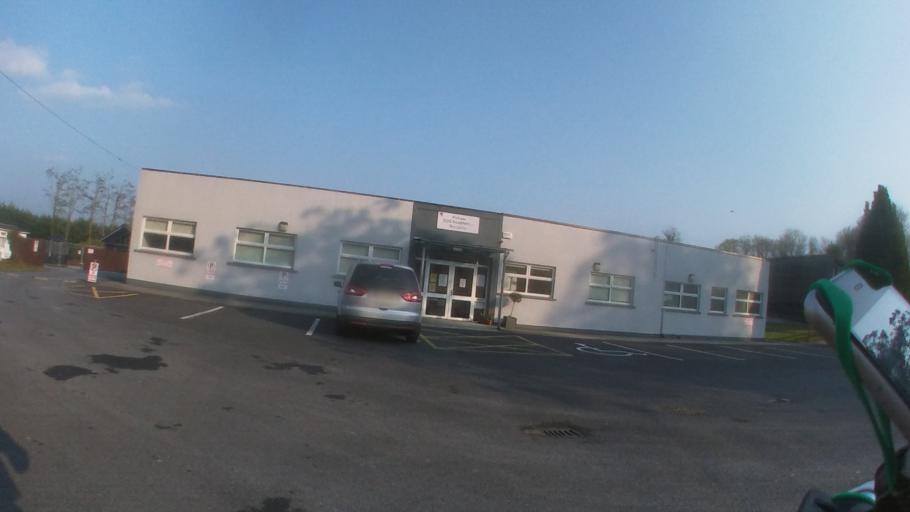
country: IE
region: Leinster
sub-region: Kilkenny
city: Kilkenny
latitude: 52.6374
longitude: -7.2692
